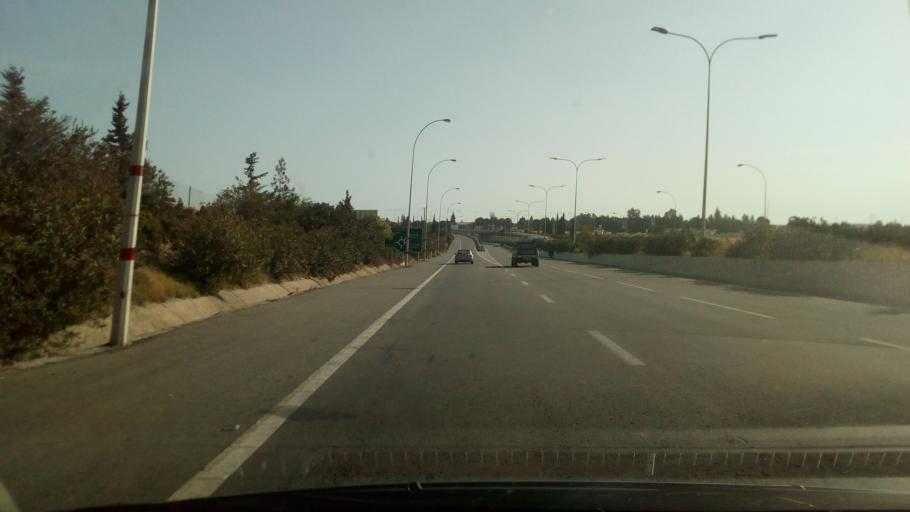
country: CY
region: Larnaka
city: Dhromolaxia
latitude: 34.9120
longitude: 33.5683
